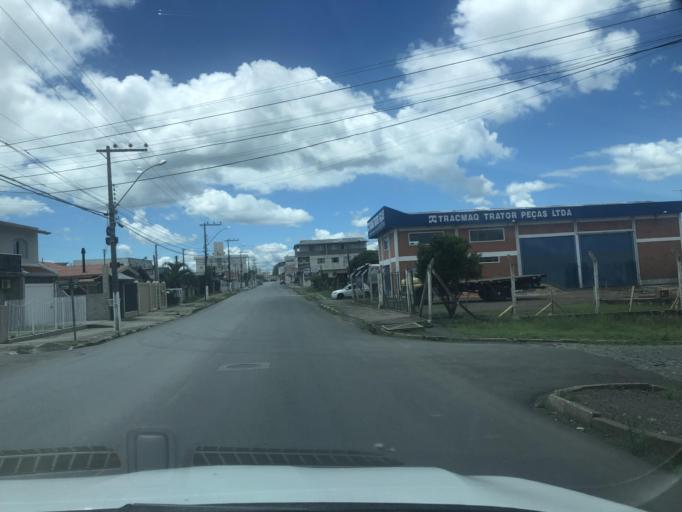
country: BR
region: Santa Catarina
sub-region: Lages
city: Lages
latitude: -27.8017
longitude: -50.3019
